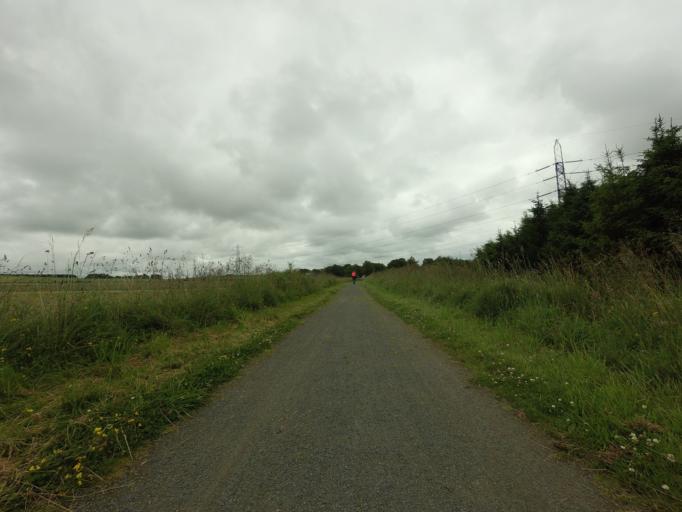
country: GB
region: Scotland
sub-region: Aberdeenshire
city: Mintlaw
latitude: 57.4935
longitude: -2.1366
